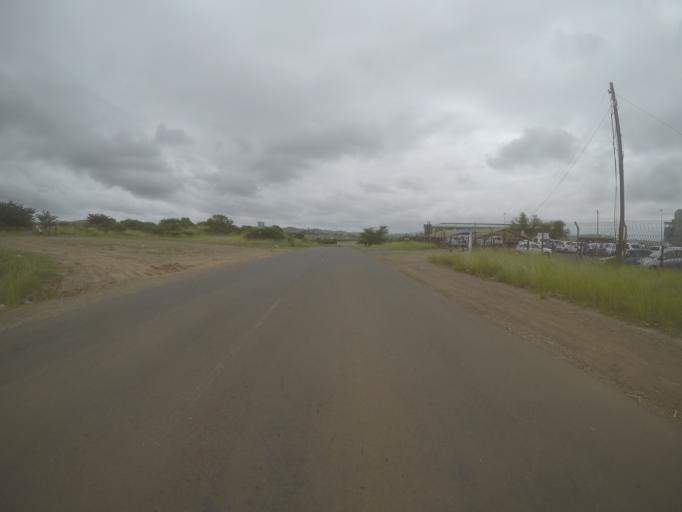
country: ZA
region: KwaZulu-Natal
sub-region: uThungulu District Municipality
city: Empangeni
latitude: -28.7209
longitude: 31.8678
